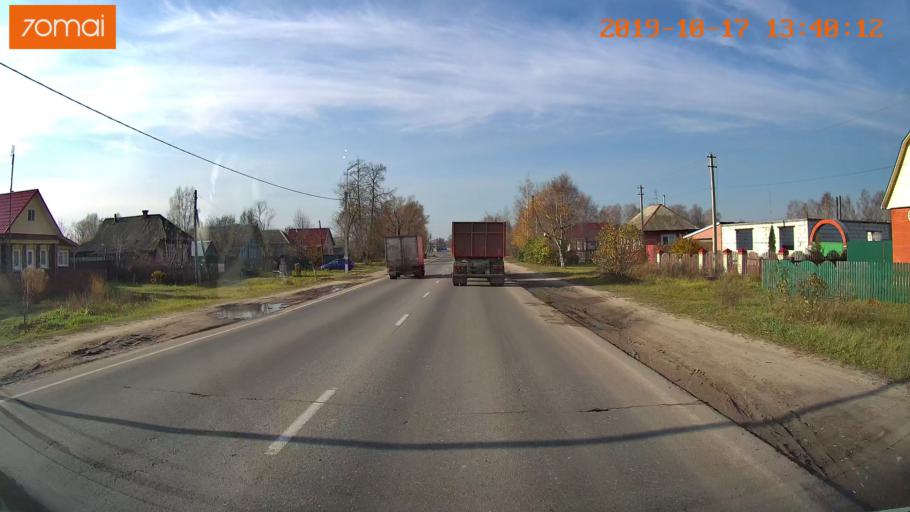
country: RU
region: Rjazan
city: Tuma
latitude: 55.1474
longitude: 40.5760
